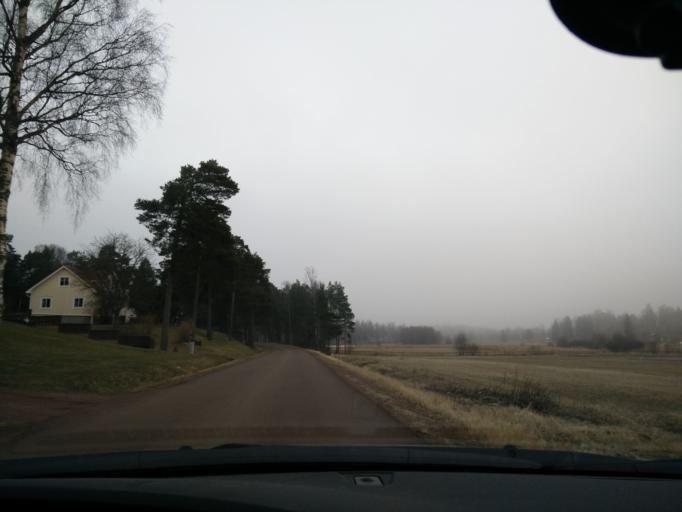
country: AX
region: Mariehamns stad
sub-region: Mariehamn
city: Mariehamn
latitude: 60.1281
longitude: 19.9199
